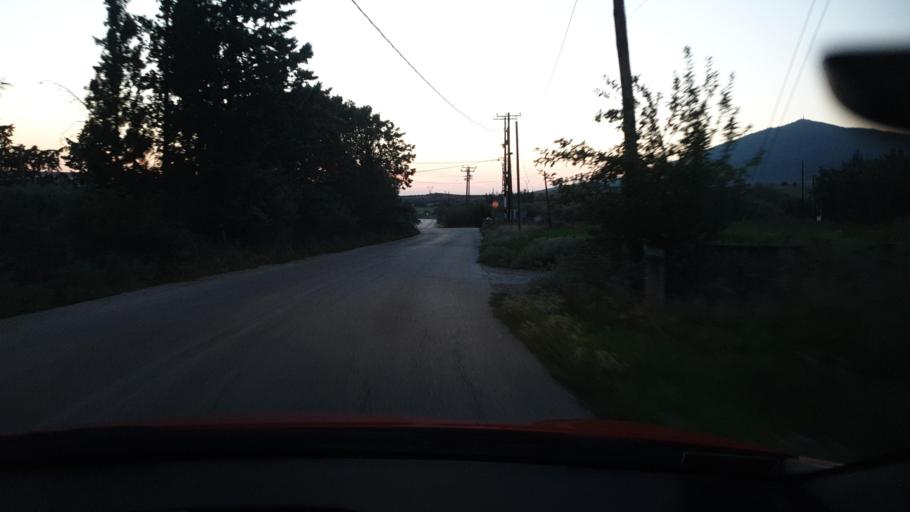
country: GR
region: Central Macedonia
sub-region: Nomos Thessalonikis
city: Vasilika
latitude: 40.5091
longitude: 23.1367
